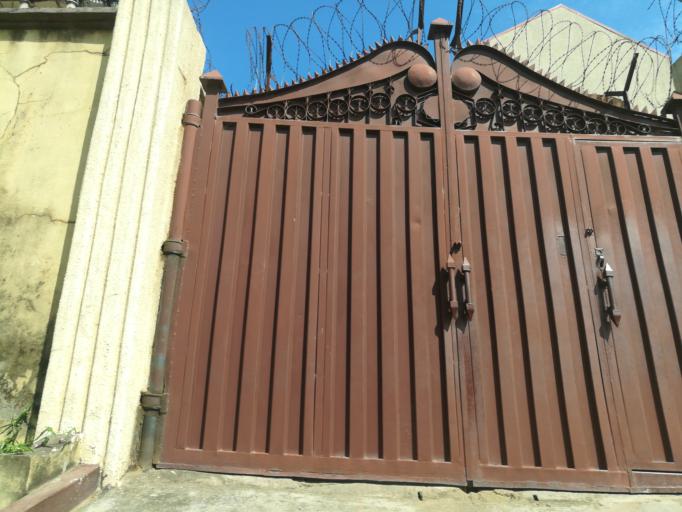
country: NG
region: Lagos
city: Ikorodu
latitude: 6.6036
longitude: 3.5038
